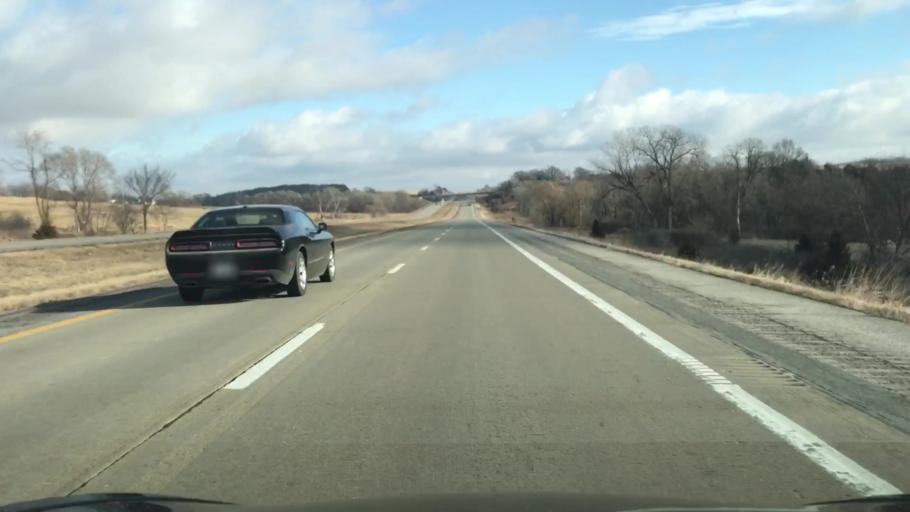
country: US
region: Iowa
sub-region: Cass County
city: Atlantic
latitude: 41.4970
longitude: -94.8445
